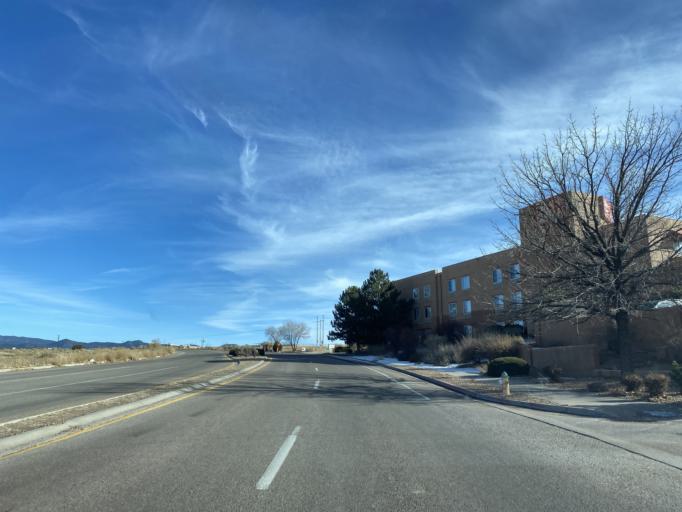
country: US
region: New Mexico
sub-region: Santa Fe County
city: Agua Fria
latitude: 35.6130
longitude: -106.0326
